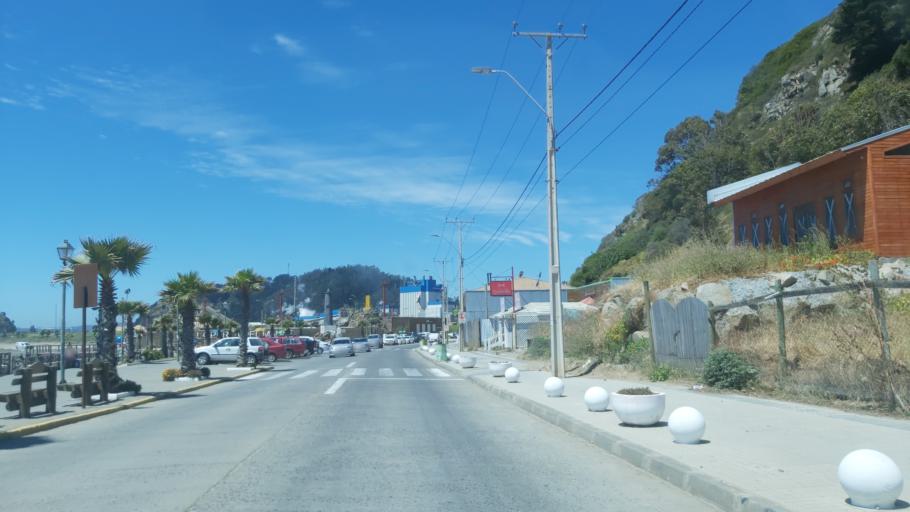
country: CL
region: Maule
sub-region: Provincia de Talca
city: Constitucion
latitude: -35.3260
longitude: -72.4265
